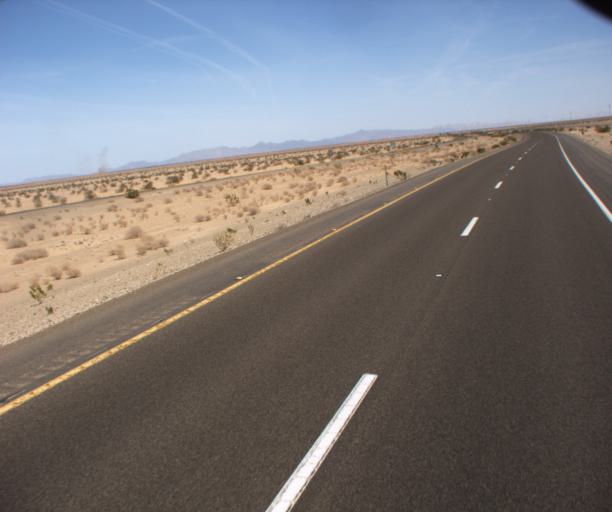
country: US
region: Arizona
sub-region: Yuma County
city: Somerton
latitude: 32.4957
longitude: -114.6442
